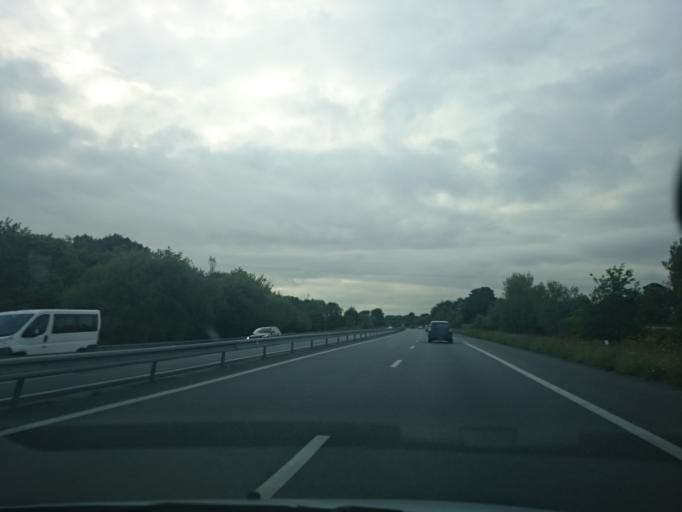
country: FR
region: Brittany
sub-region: Departement du Morbihan
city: Brech
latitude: 47.6970
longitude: -3.0377
